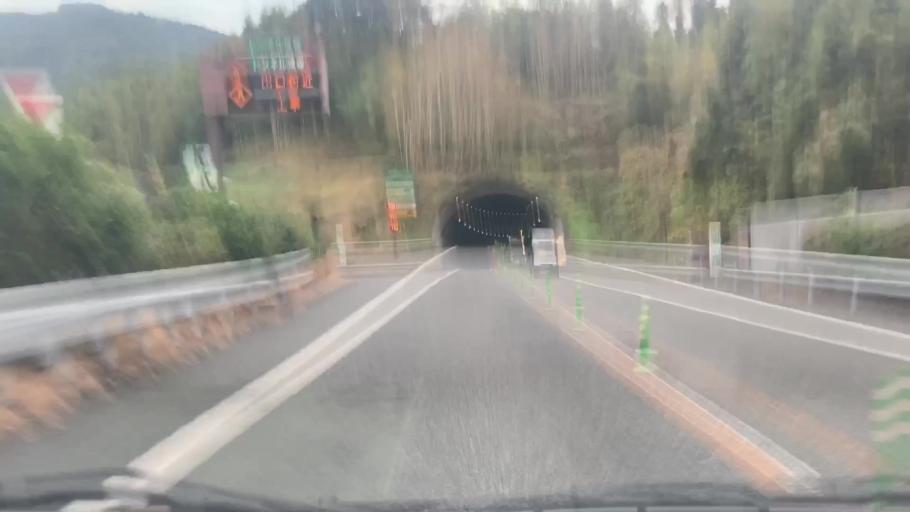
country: JP
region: Nagasaki
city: Obita
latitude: 32.7993
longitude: 129.9648
